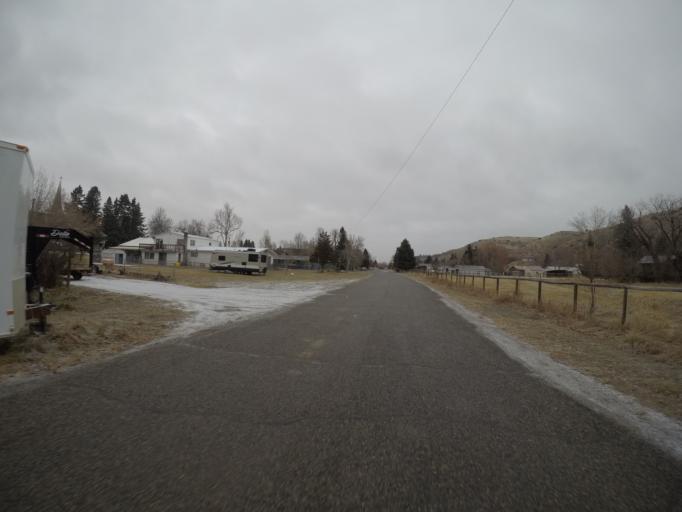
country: US
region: Montana
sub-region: Stillwater County
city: Absarokee
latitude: 45.5149
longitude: -109.4444
